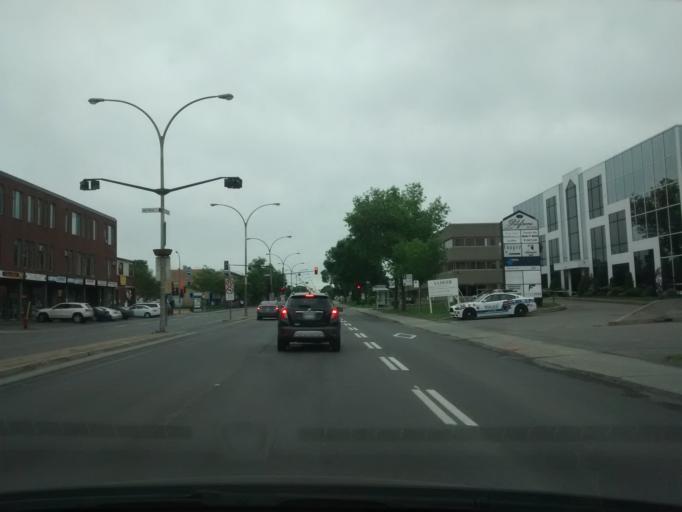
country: CA
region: Quebec
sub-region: Montreal
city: Saint-Leonard
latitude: 45.5782
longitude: -73.6179
